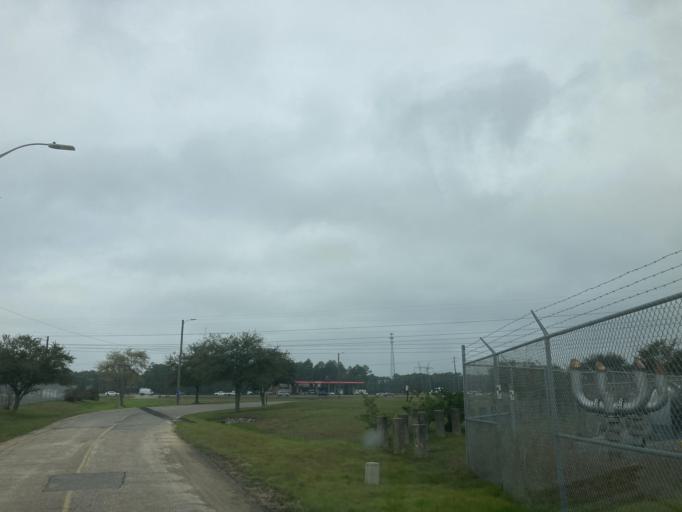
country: US
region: Mississippi
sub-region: Harrison County
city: West Gulfport
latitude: 30.4384
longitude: -89.0288
